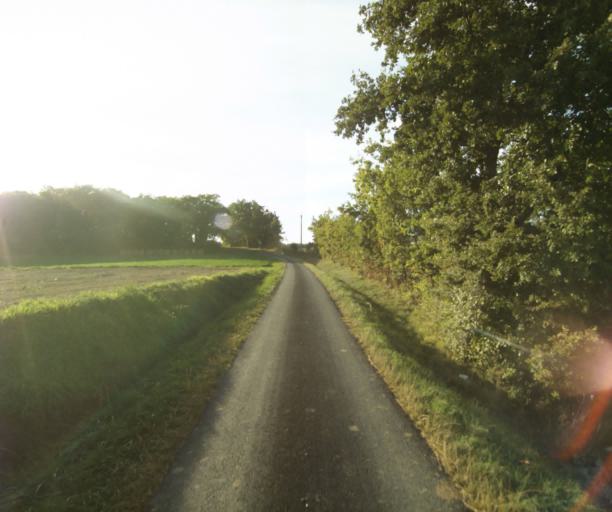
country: FR
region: Midi-Pyrenees
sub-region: Departement du Gers
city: Gondrin
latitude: 43.8899
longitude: 0.2608
